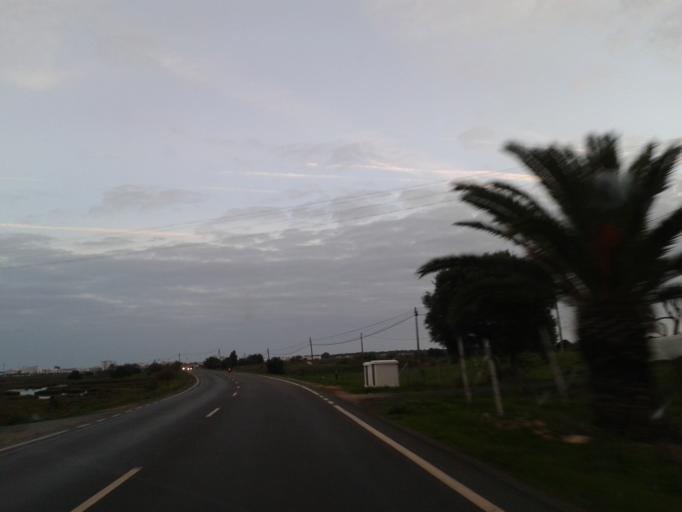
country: PT
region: Faro
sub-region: Castro Marim
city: Castro Marim
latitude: 37.2097
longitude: -7.4370
